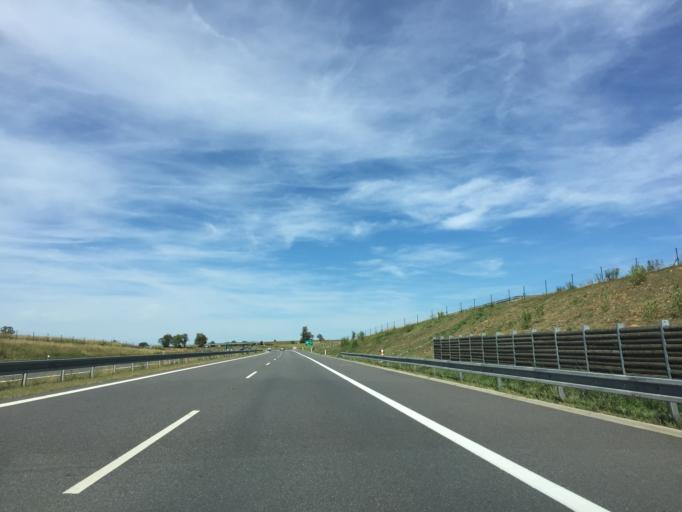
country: CZ
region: Jihocesky
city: Sobeslav
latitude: 49.2523
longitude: 14.7338
